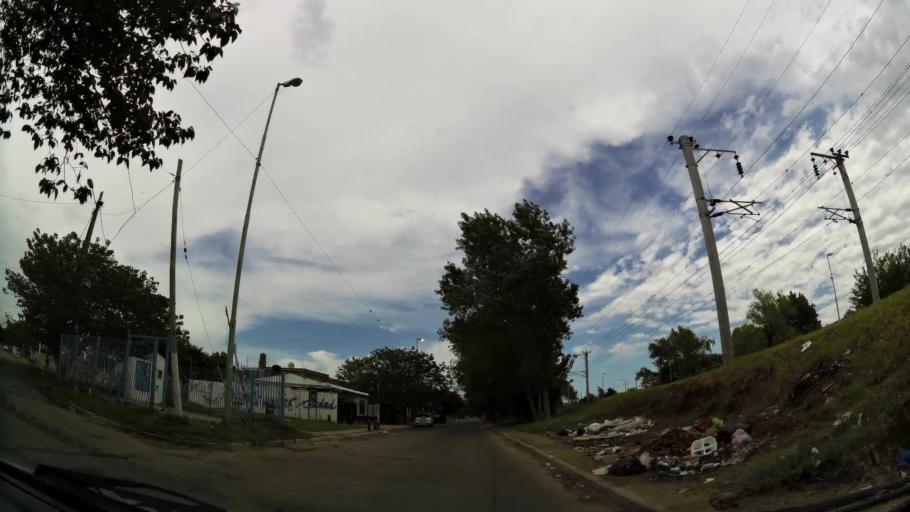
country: AR
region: Buenos Aires
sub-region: Partido de Quilmes
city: Quilmes
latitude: -34.7558
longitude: -58.2263
